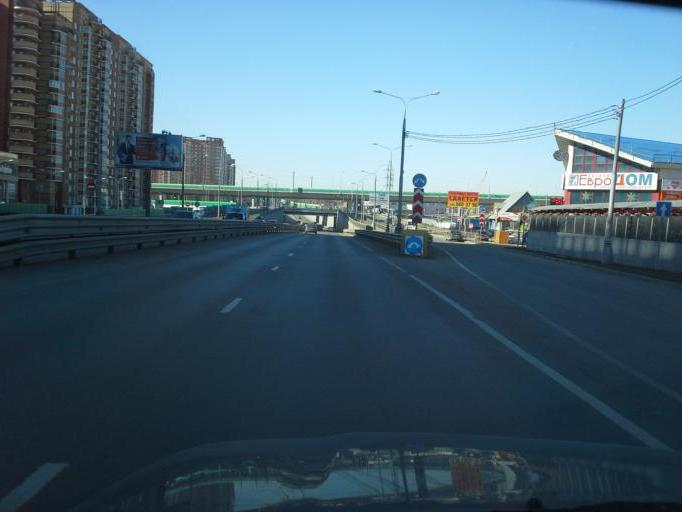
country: RU
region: Moskovskaya
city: Lesnoy Gorodok
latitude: 55.6611
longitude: 37.2292
